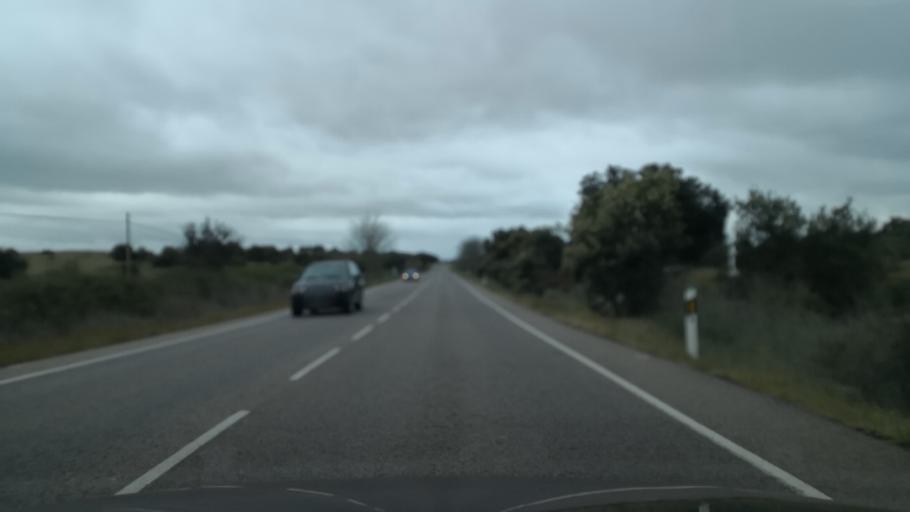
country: ES
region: Extremadura
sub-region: Provincia de Caceres
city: Caceres
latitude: 39.4163
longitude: -6.4138
